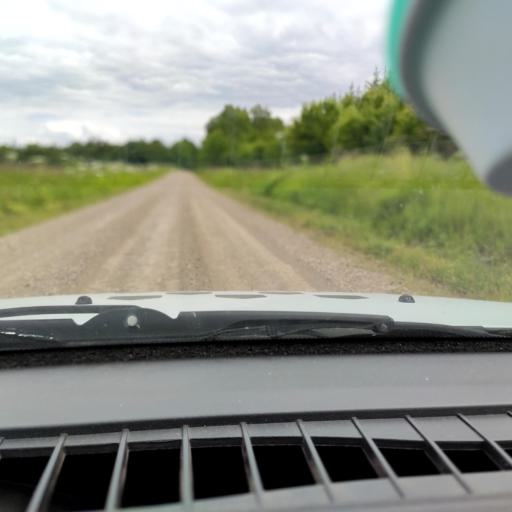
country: RU
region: Perm
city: Suksun
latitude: 57.2092
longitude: 57.6464
